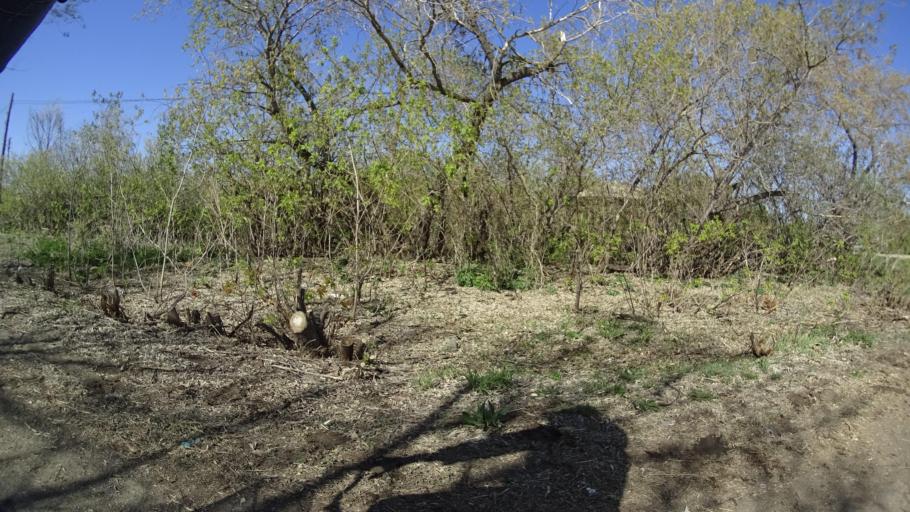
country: RU
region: Chelyabinsk
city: Chesma
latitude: 53.7966
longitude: 61.0255
